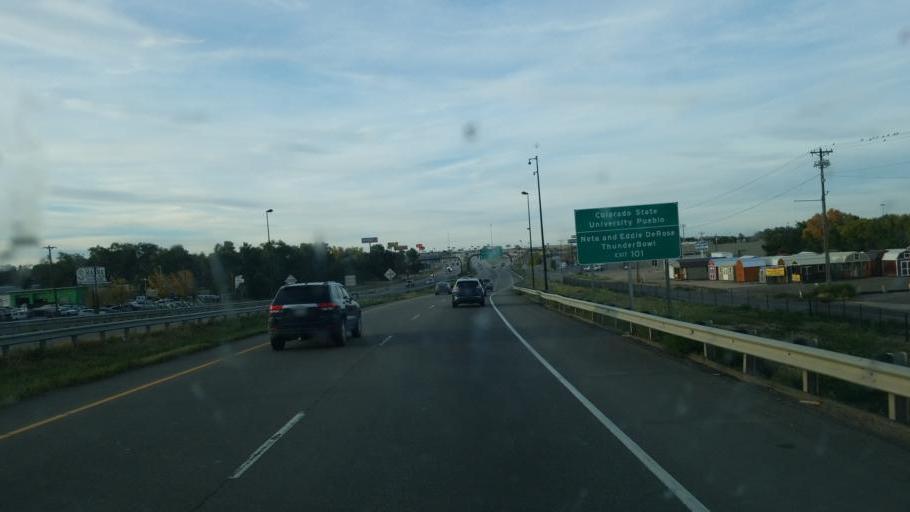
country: US
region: Colorado
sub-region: Pueblo County
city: Pueblo
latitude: 38.2989
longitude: -104.6118
